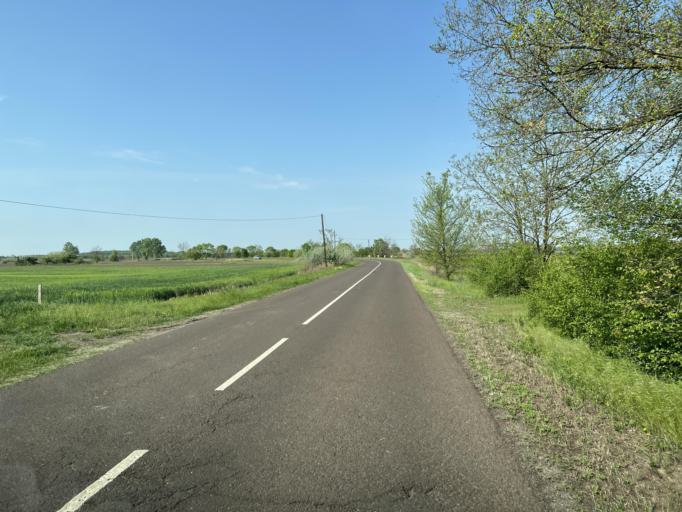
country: HU
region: Pest
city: Jaszkarajeno
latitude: 47.0341
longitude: 20.0351
